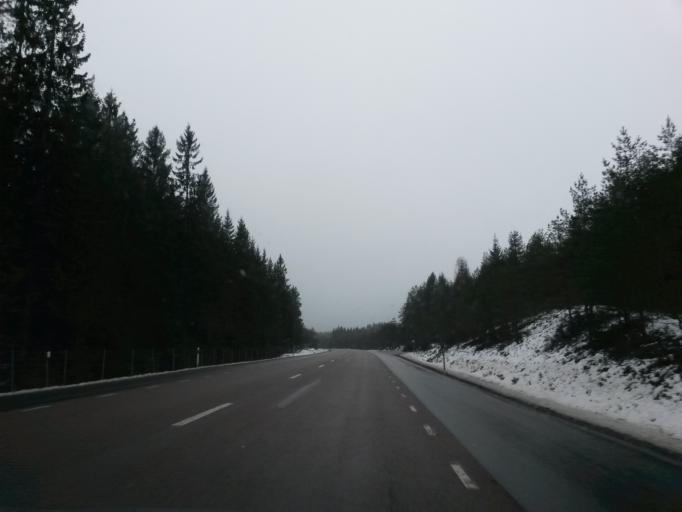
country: SE
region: Vaestra Goetaland
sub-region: Boras Kommun
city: Viskafors
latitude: 57.6248
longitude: 12.8880
